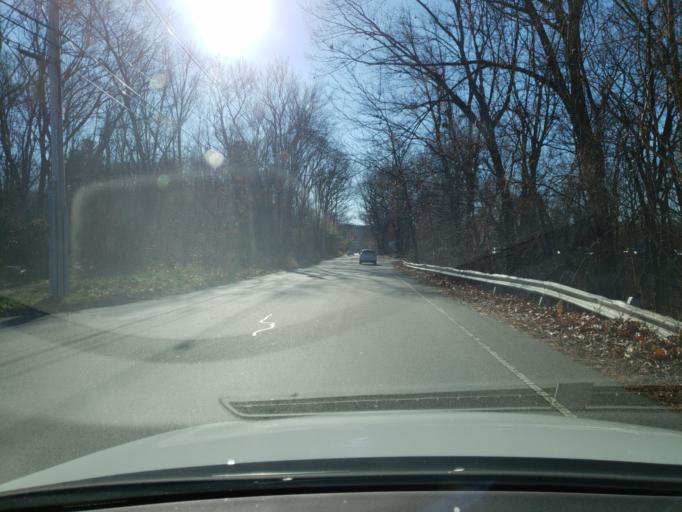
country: US
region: Massachusetts
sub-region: Essex County
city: Andover
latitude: 42.6776
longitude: -71.1342
